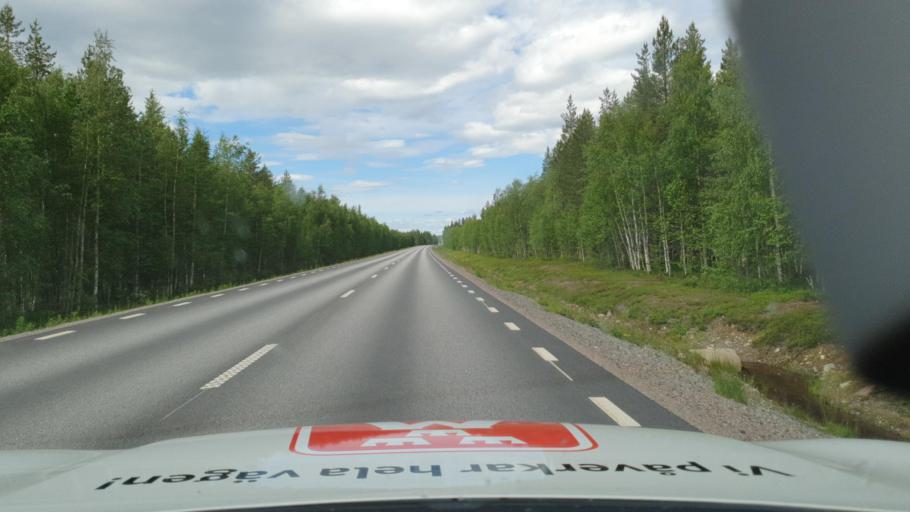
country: SE
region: Vaesterbotten
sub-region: Norsjo Kommun
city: Norsjoe
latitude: 65.1787
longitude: 19.8568
